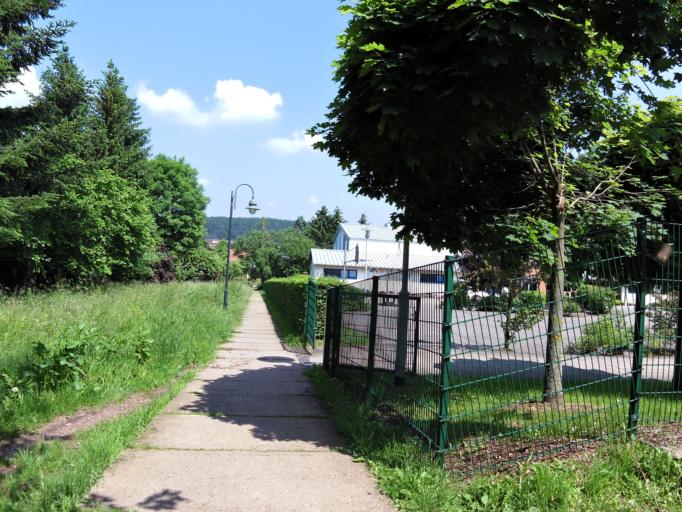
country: DE
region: Thuringia
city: Friedrichroda
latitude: 50.8553
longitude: 10.5748
